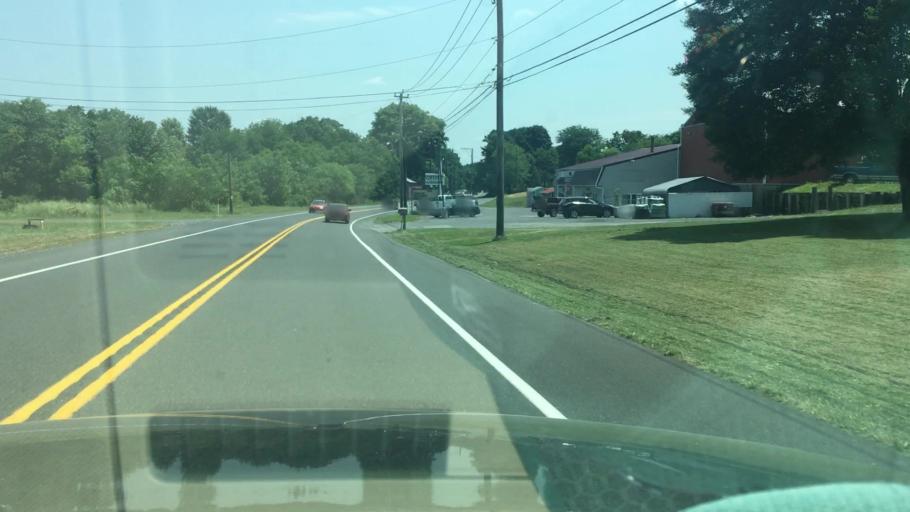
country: US
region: Pennsylvania
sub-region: Lehigh County
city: Schnecksville
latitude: 40.6801
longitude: -75.7069
